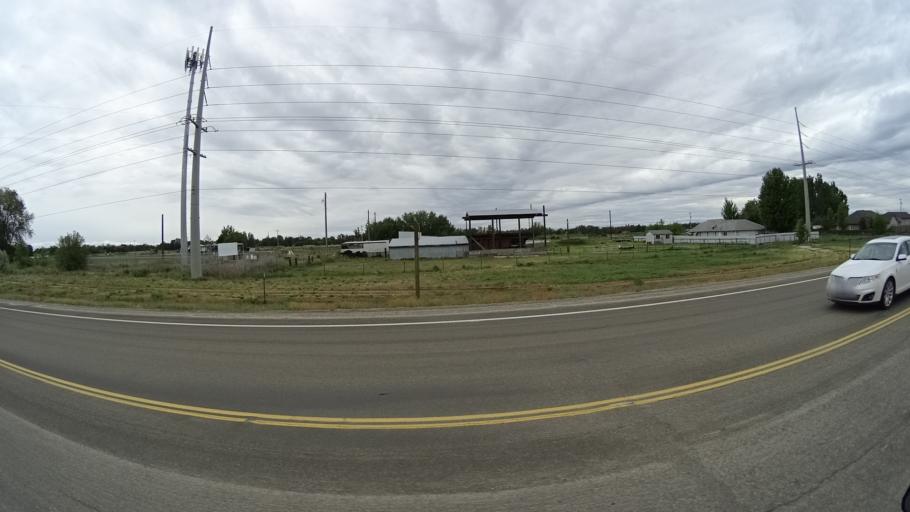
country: US
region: Idaho
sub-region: Ada County
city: Star
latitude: 43.6919
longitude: -116.4556
